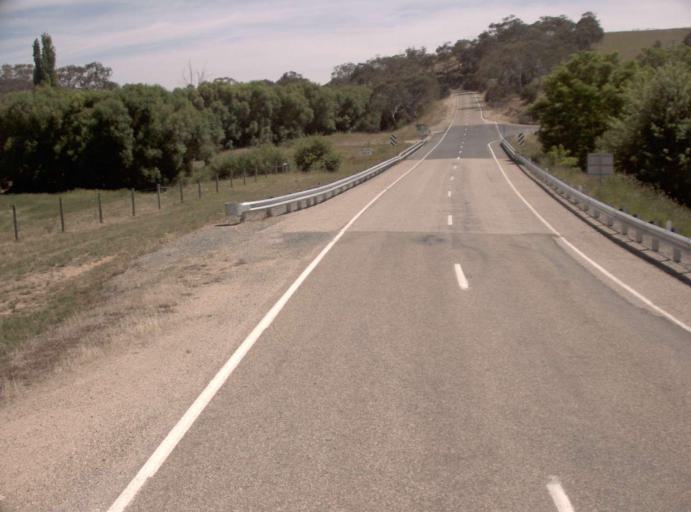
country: AU
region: Victoria
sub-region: Alpine
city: Mount Beauty
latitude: -37.0669
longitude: 147.6030
